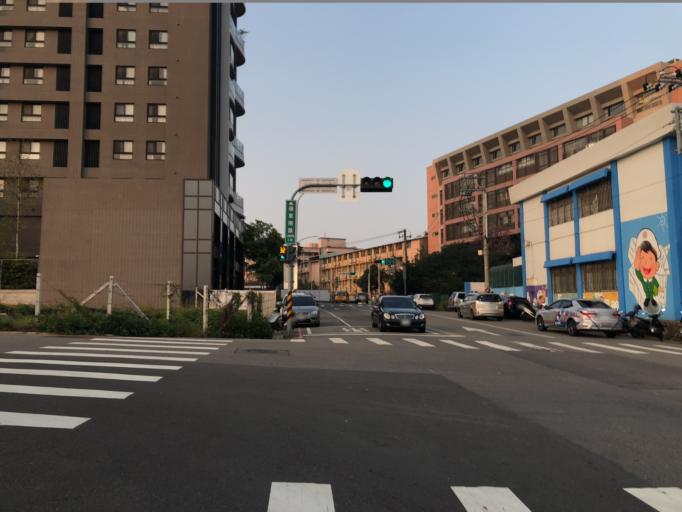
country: TW
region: Taiwan
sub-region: Taichung City
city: Taichung
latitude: 24.1356
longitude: 120.6103
